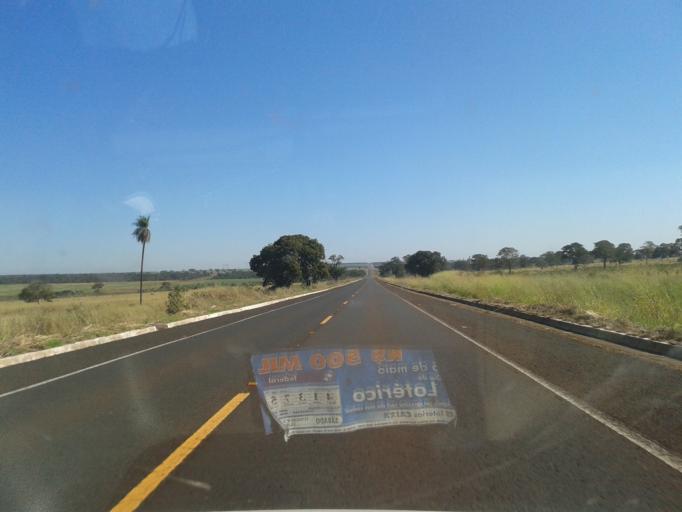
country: BR
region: Minas Gerais
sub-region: Santa Vitoria
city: Santa Vitoria
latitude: -19.0875
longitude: -50.3497
